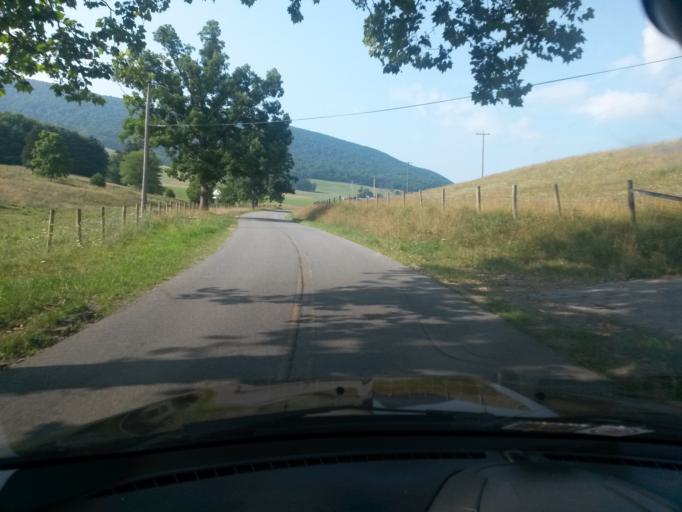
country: US
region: Virginia
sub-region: Giles County
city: Narrows
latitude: 37.3846
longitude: -80.7911
